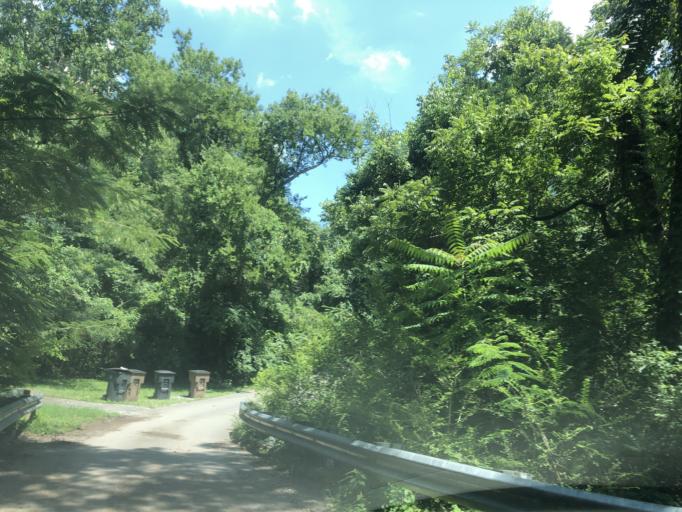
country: US
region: Tennessee
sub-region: Davidson County
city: Lakewood
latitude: 36.1706
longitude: -86.6597
